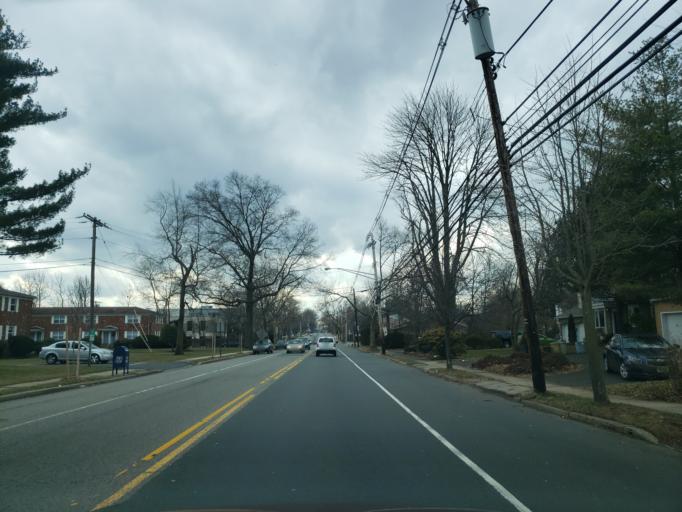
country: US
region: New Jersey
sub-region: Union County
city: Springfield
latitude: 40.6886
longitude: -74.3336
